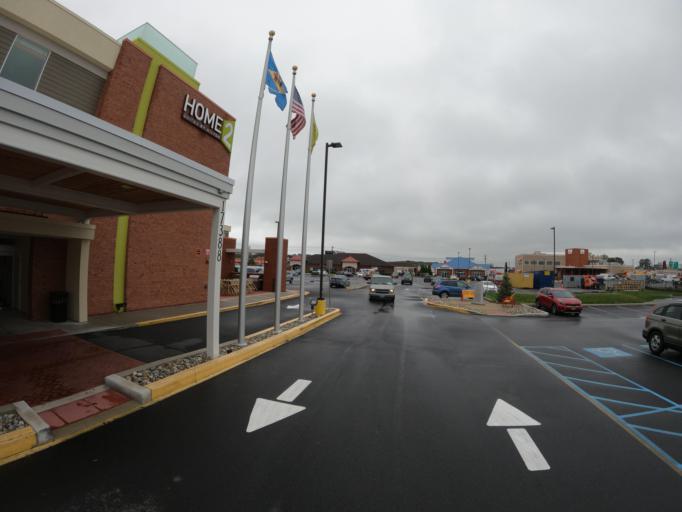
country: US
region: Delaware
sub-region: Sussex County
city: Lewes
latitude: 38.7504
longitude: -75.1656
